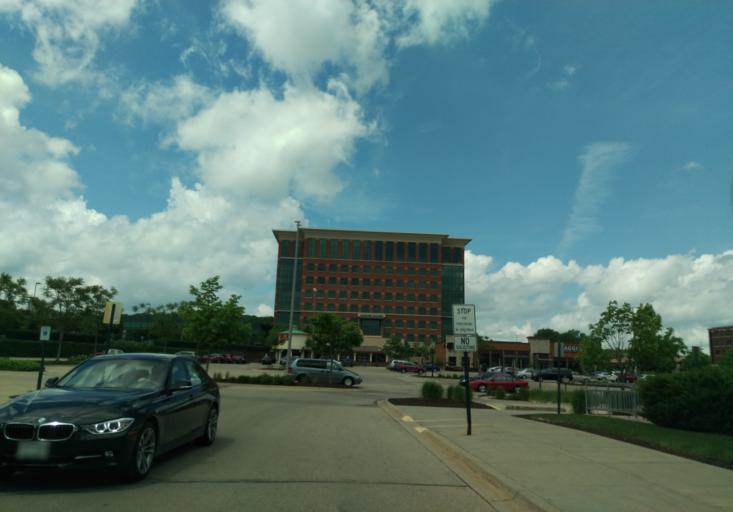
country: US
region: Wisconsin
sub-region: Dane County
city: Middleton
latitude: 43.0907
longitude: -89.5275
